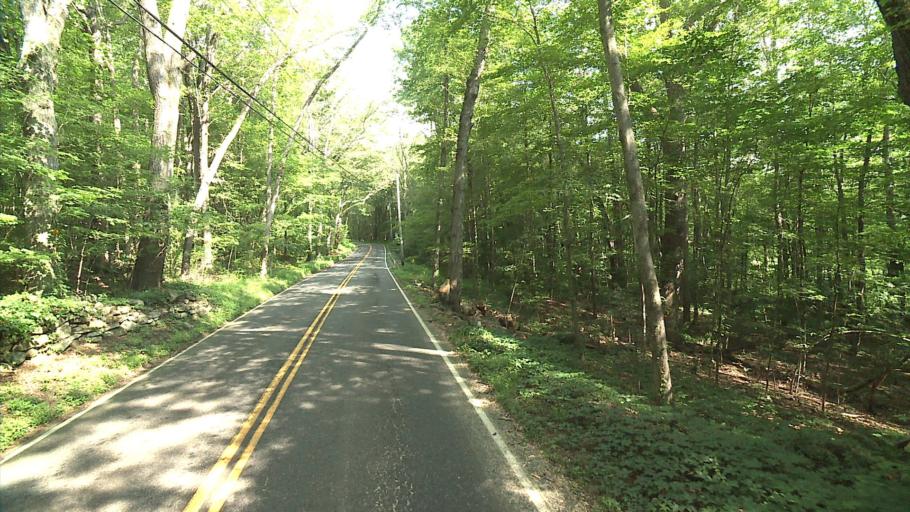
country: US
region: Connecticut
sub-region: Middlesex County
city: Chester Center
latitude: 41.3761
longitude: -72.5050
